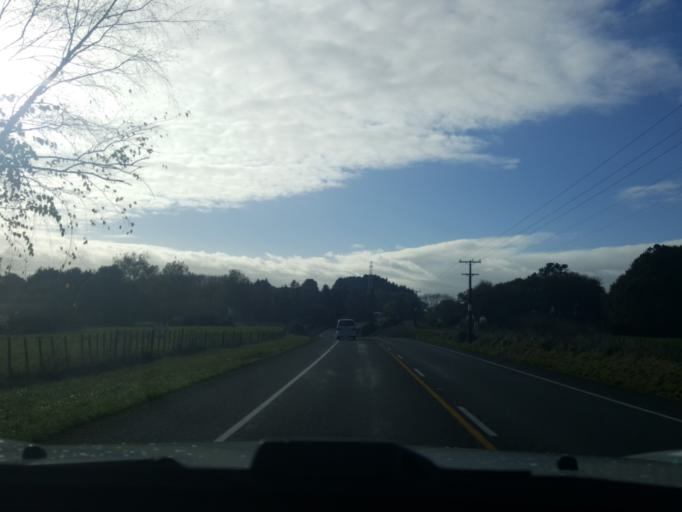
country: NZ
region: Waikato
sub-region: Waipa District
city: Cambridge
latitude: -37.6661
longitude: 175.4965
